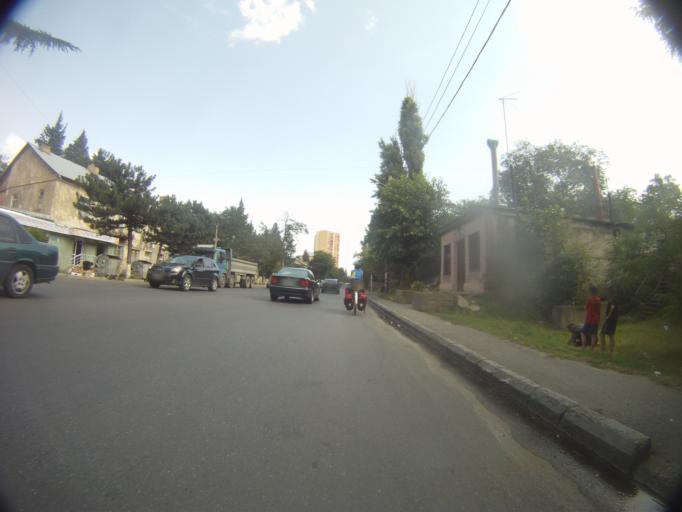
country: GE
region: T'bilisi
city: Tbilisi
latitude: 41.6506
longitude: 44.9075
